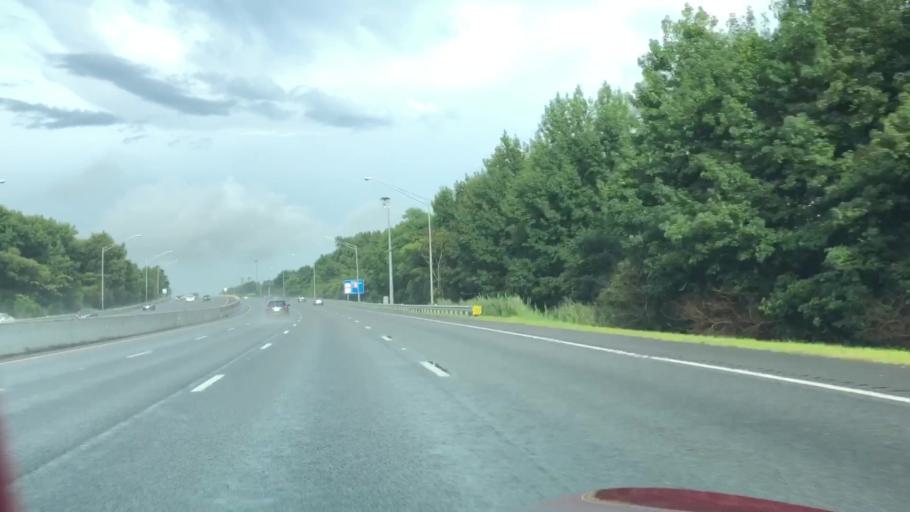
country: US
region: Virginia
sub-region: City of Virginia Beach
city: Virginia Beach
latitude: 36.8424
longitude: -76.0354
